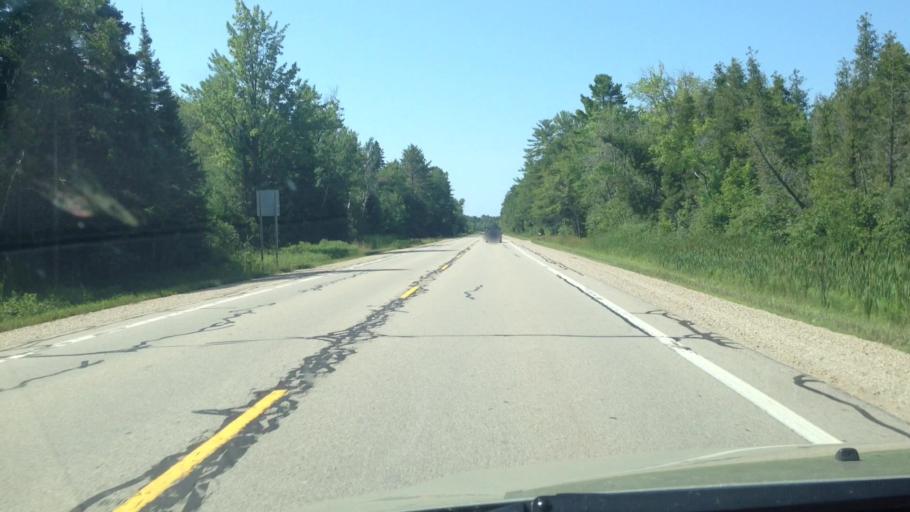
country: US
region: Michigan
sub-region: Menominee County
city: Menominee
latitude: 45.3904
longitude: -87.3706
